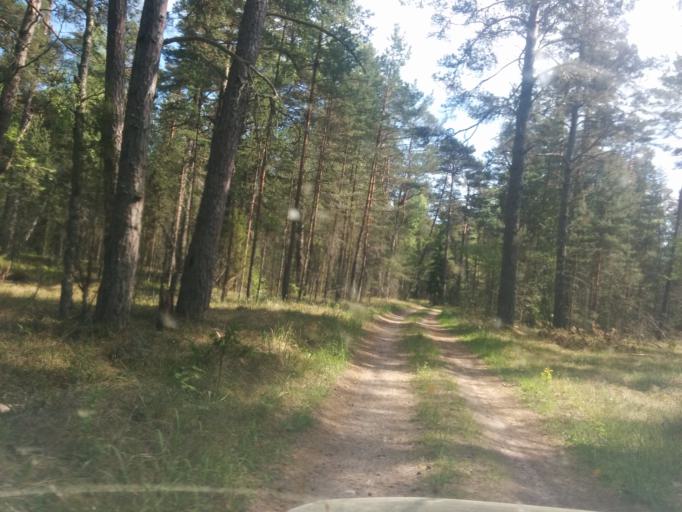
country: LV
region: Dundaga
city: Dundaga
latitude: 57.6191
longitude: 22.0849
